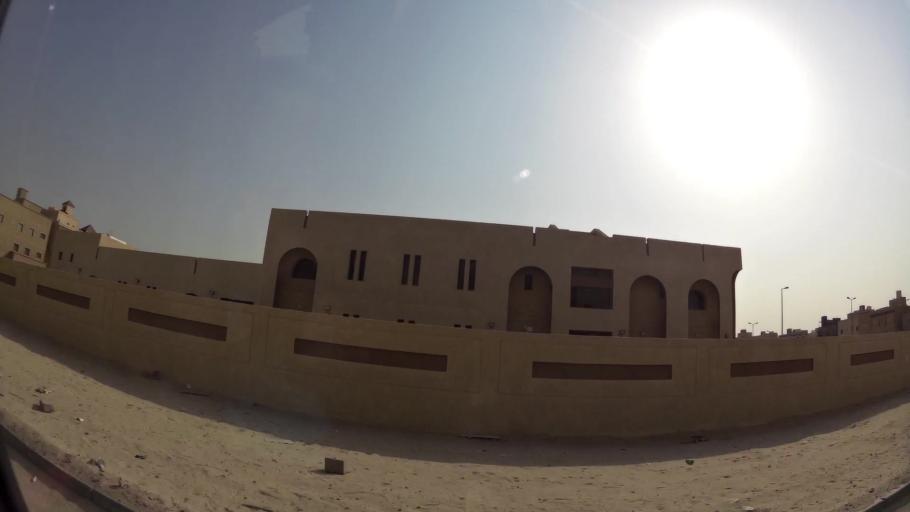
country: KW
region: Al Asimah
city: Ar Rabiyah
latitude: 29.3288
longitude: 47.8043
